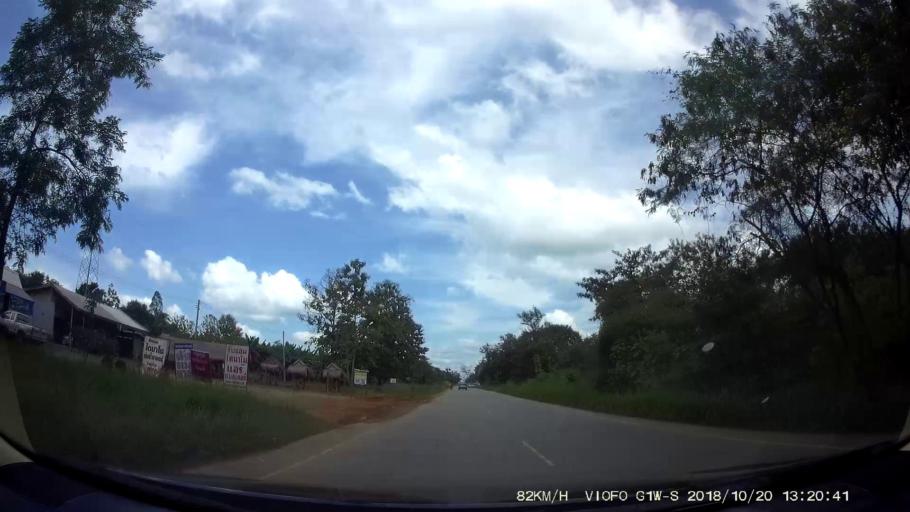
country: TH
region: Chaiyaphum
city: Khon San
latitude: 16.5509
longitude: 101.9055
